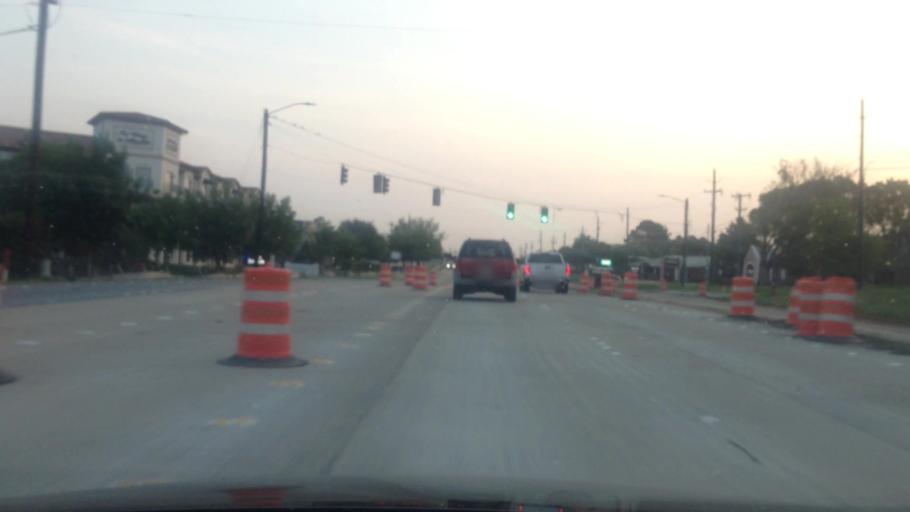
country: US
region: Texas
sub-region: Tarrant County
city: Colleyville
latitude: 32.8850
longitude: -97.1529
